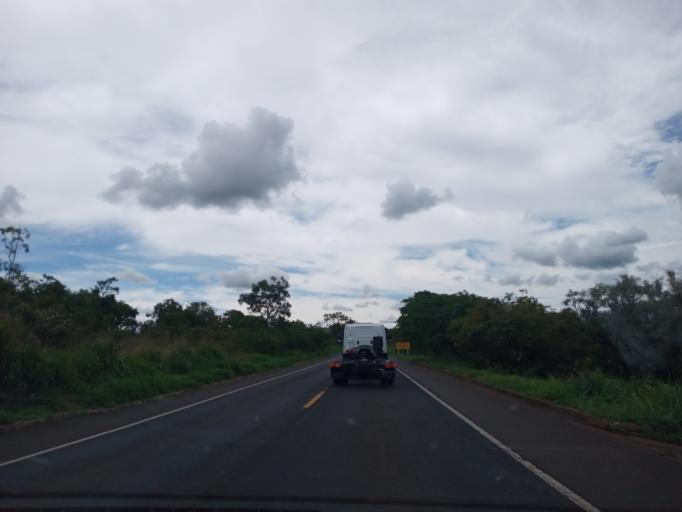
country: BR
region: Minas Gerais
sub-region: Uberlandia
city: Uberlandia
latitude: -19.1839
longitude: -47.8774
